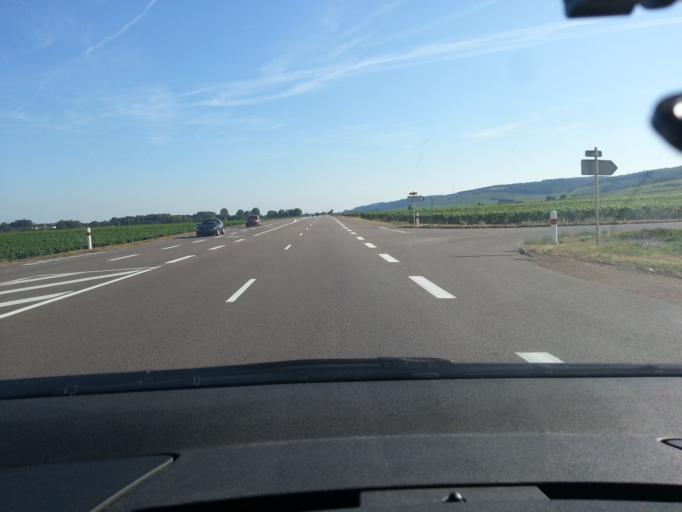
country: FR
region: Bourgogne
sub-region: Departement de la Cote-d'Or
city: Gevrey-Chambertin
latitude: 47.1878
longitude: 4.9677
